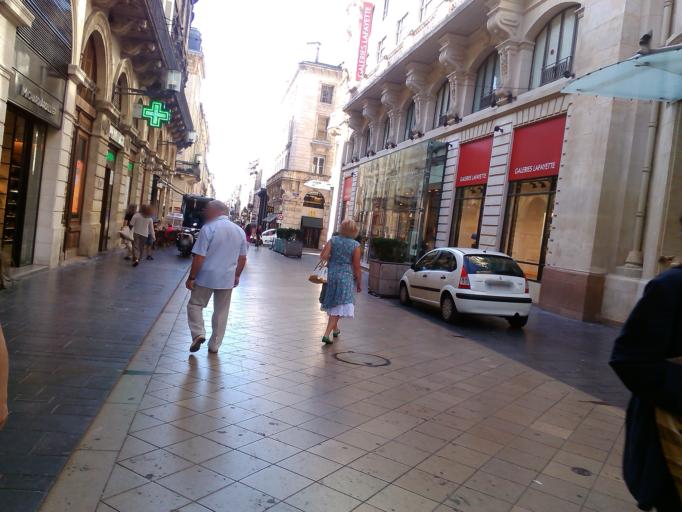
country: FR
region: Aquitaine
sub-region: Departement de la Gironde
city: Bordeaux
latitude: 44.8416
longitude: -0.5745
